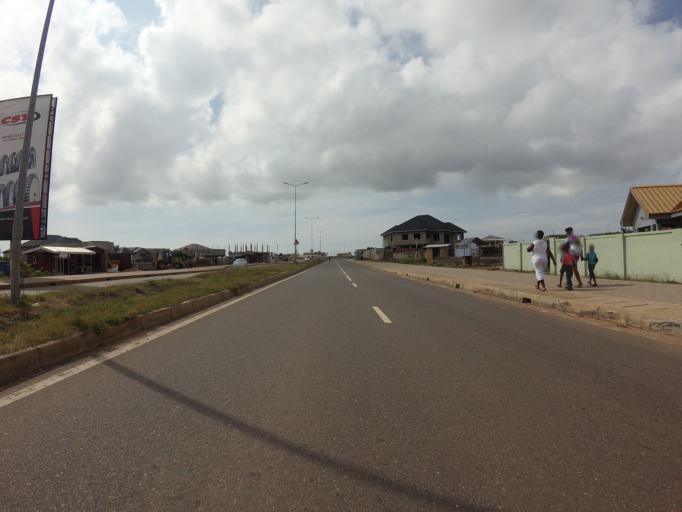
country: GH
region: Greater Accra
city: Teshi Old Town
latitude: 5.5972
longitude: -0.1353
